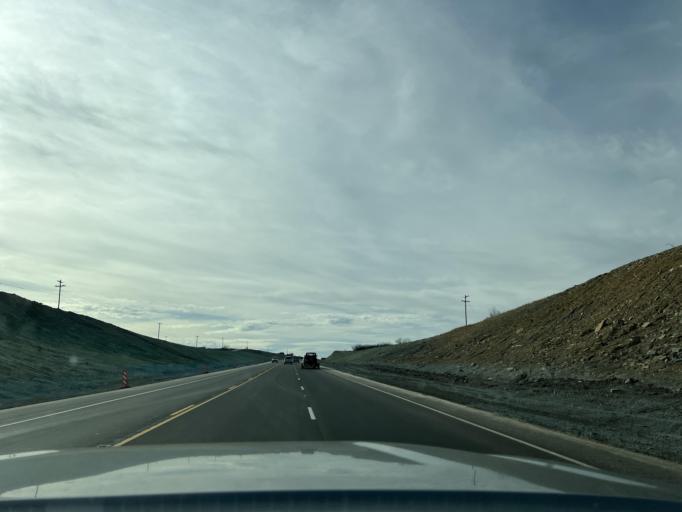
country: US
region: Texas
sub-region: Shackelford County
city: Albany
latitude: 32.7079
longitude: -99.3756
